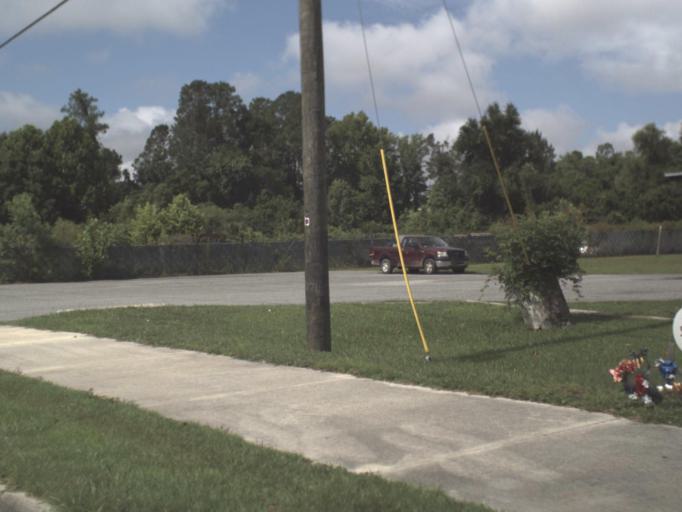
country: US
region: Florida
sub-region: Columbia County
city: Five Points
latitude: 30.2120
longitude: -82.6378
